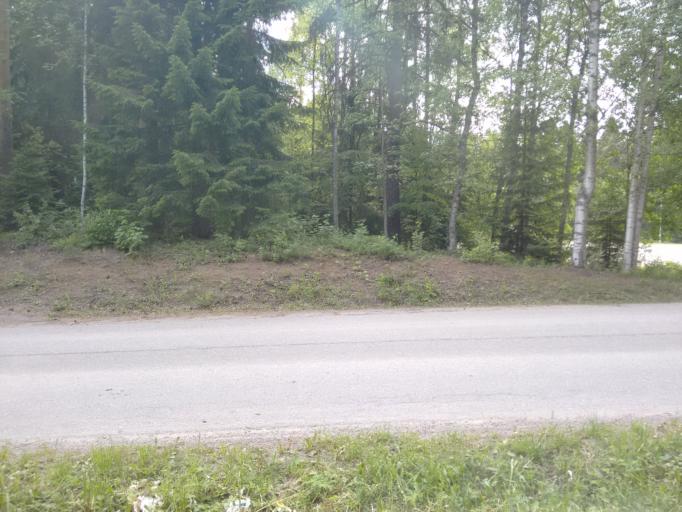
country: FI
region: Pirkanmaa
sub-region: Tampere
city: Tampere
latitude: 61.5095
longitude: 23.7946
